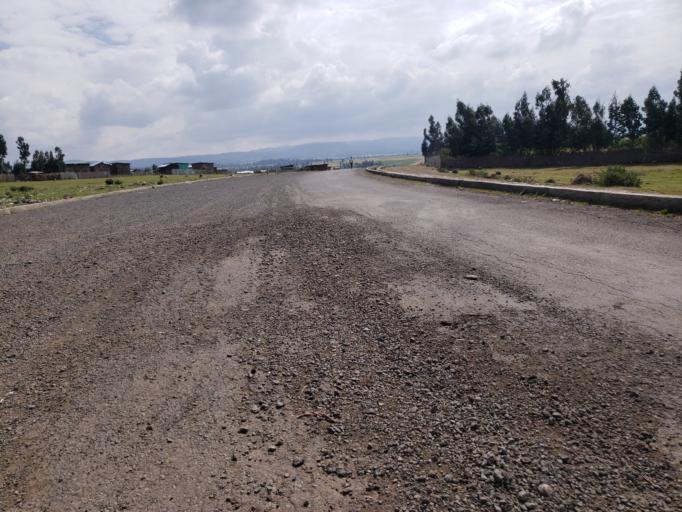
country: ET
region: Oromiya
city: Dodola
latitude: 6.9970
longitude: 39.3913
